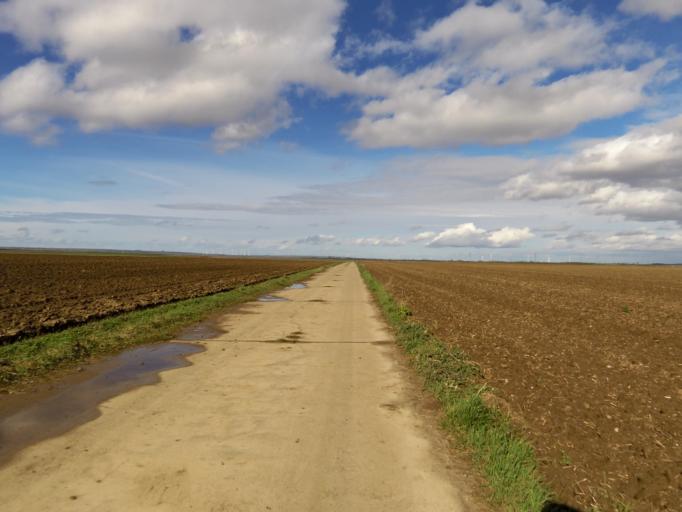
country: DE
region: Rheinland-Pfalz
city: Dirmstein
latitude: 49.5834
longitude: 8.2611
